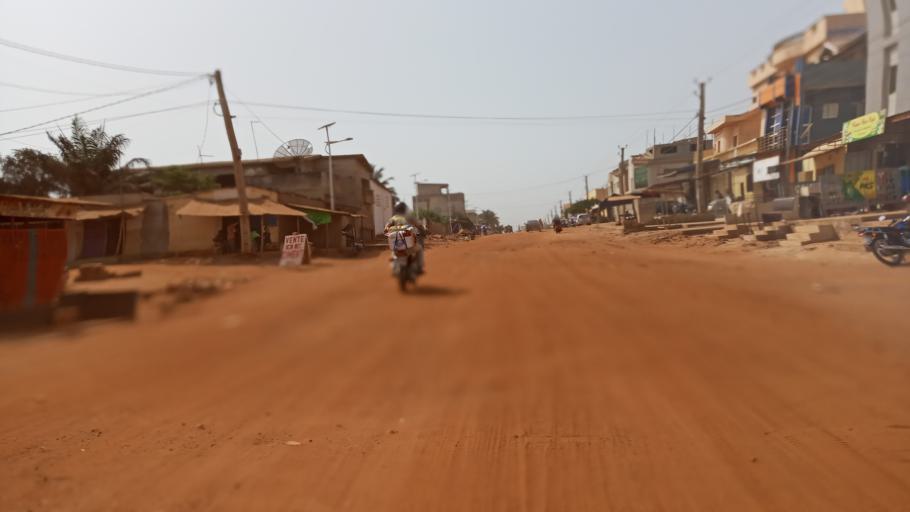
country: TG
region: Maritime
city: Lome
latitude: 6.2010
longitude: 1.1689
